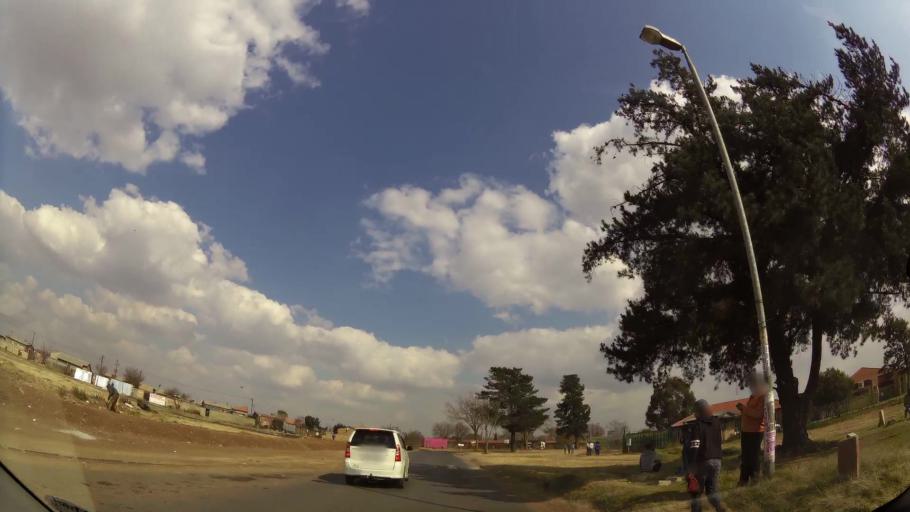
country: ZA
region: Gauteng
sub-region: Ekurhuleni Metropolitan Municipality
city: Springs
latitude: -26.1313
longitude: 28.4374
